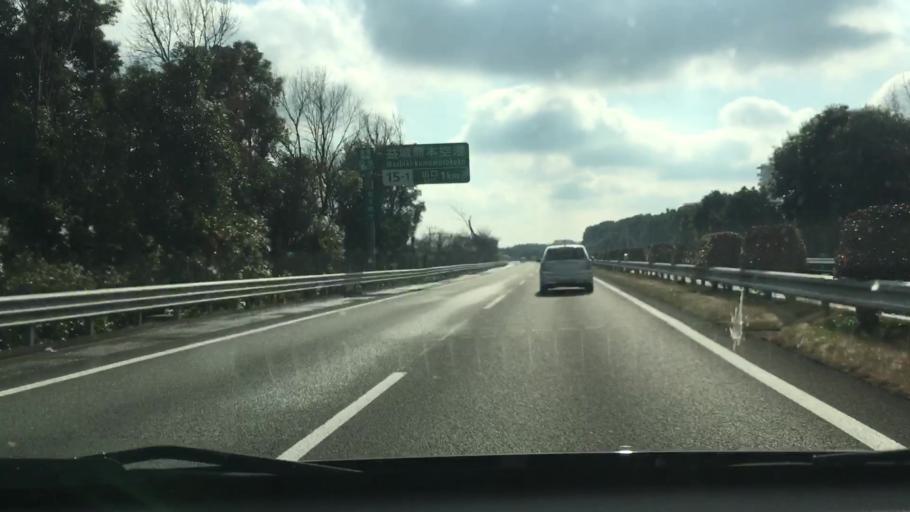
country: JP
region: Kumamoto
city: Ozu
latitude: 32.8014
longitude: 130.7917
